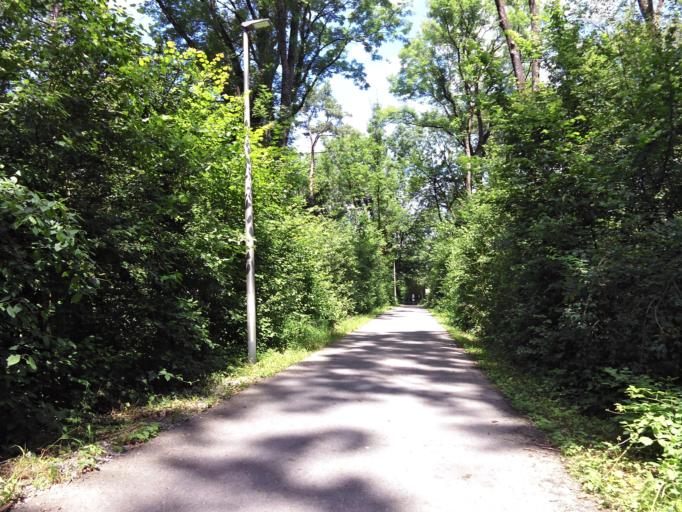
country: AT
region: Vorarlberg
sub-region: Politischer Bezirk Bregenz
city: Hard
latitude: 47.4964
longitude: 9.6990
